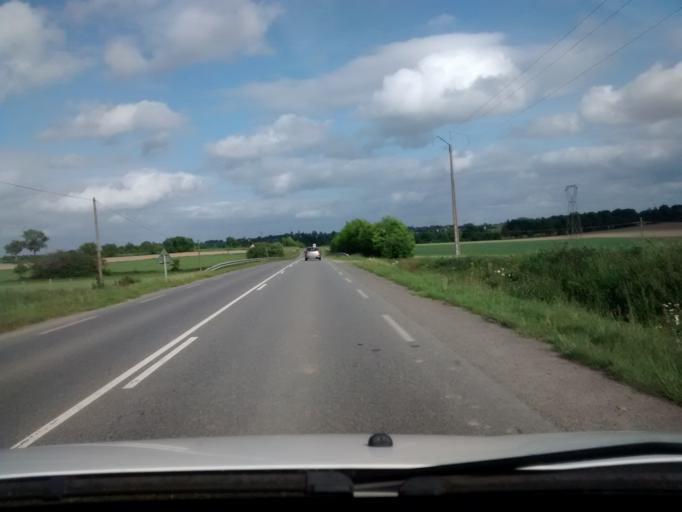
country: FR
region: Brittany
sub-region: Departement d'Ille-et-Vilaine
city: Vern-sur-Seiche
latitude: 48.0468
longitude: -1.5770
